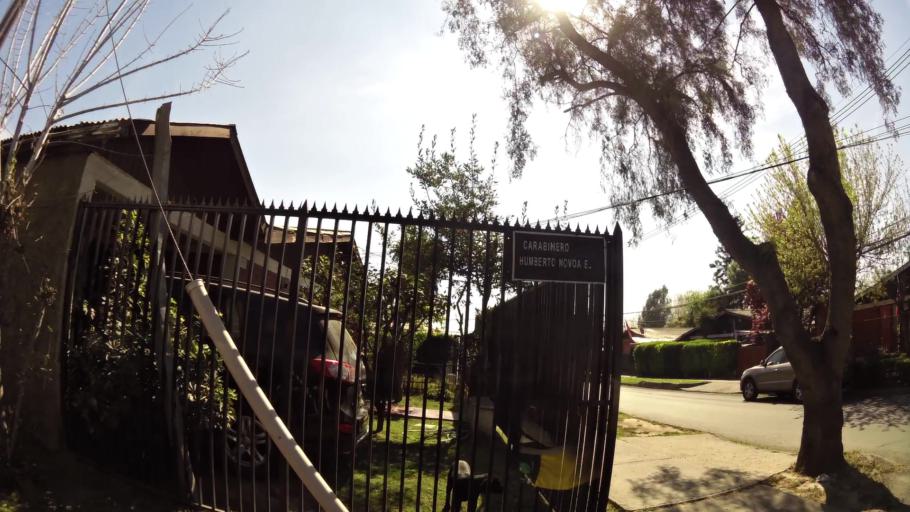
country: CL
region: Santiago Metropolitan
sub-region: Provincia de Santiago
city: Villa Presidente Frei, Nunoa, Santiago, Chile
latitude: -33.4980
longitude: -70.5802
